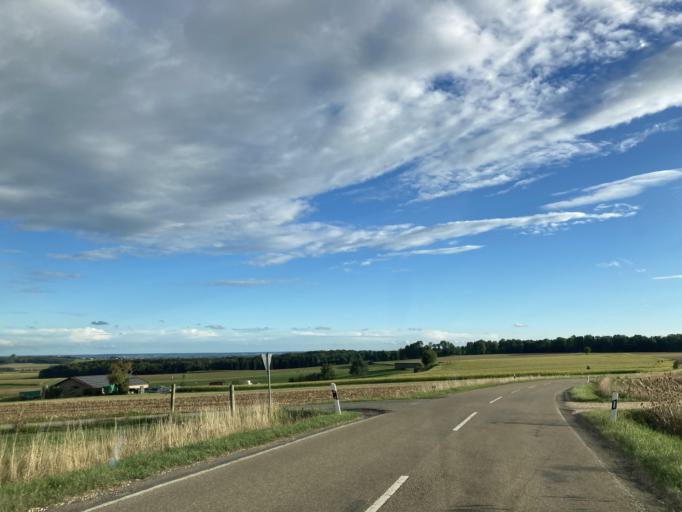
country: DE
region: Bavaria
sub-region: Swabia
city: Modingen
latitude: 48.6737
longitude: 10.4315
